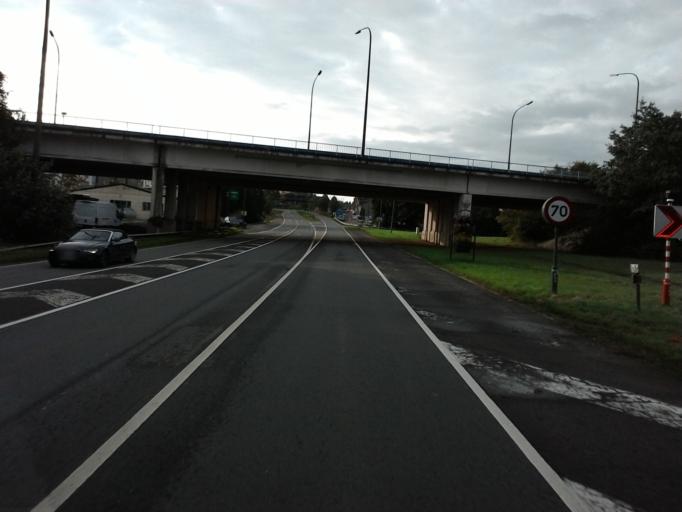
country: BE
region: Wallonia
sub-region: Province du Luxembourg
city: Arlon
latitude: 49.6986
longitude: 5.8083
